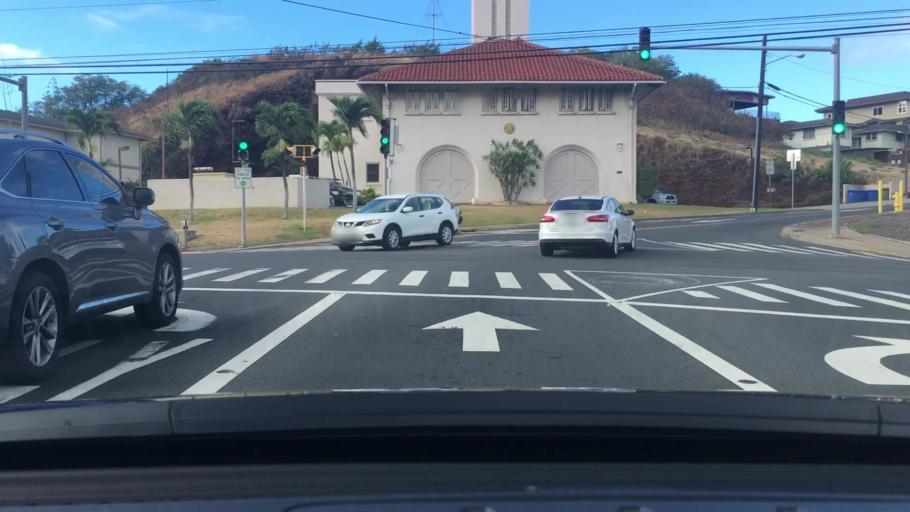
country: US
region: Hawaii
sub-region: Honolulu County
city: Honolulu
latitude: 21.2790
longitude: -157.7992
